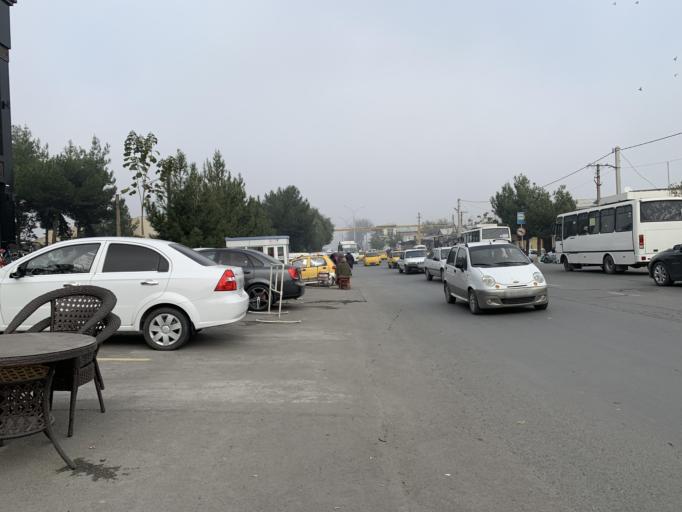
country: UZ
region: Fergana
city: Qo`qon
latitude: 40.5485
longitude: 70.9583
